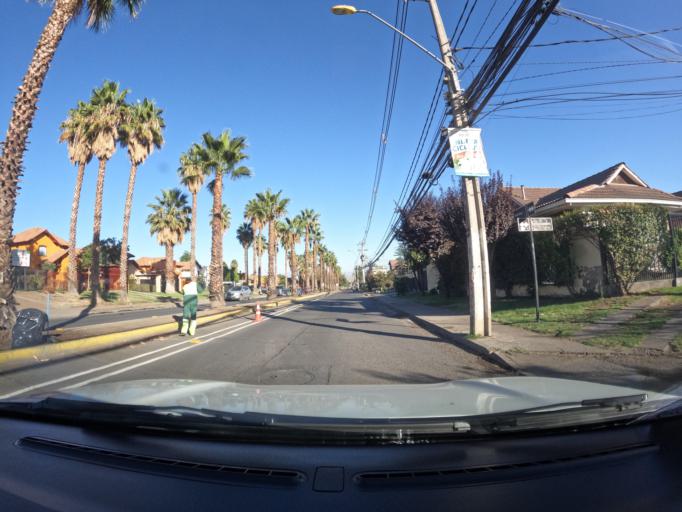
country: CL
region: Santiago Metropolitan
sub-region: Provincia de Santiago
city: Villa Presidente Frei, Nunoa, Santiago, Chile
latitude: -33.4812
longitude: -70.5510
